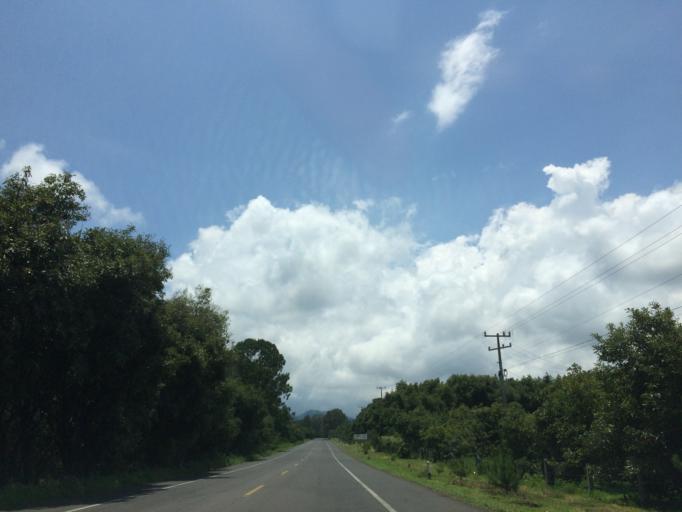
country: MX
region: Michoacan
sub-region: Periban
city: San Francisco Periban
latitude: 19.5548
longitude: -102.3893
